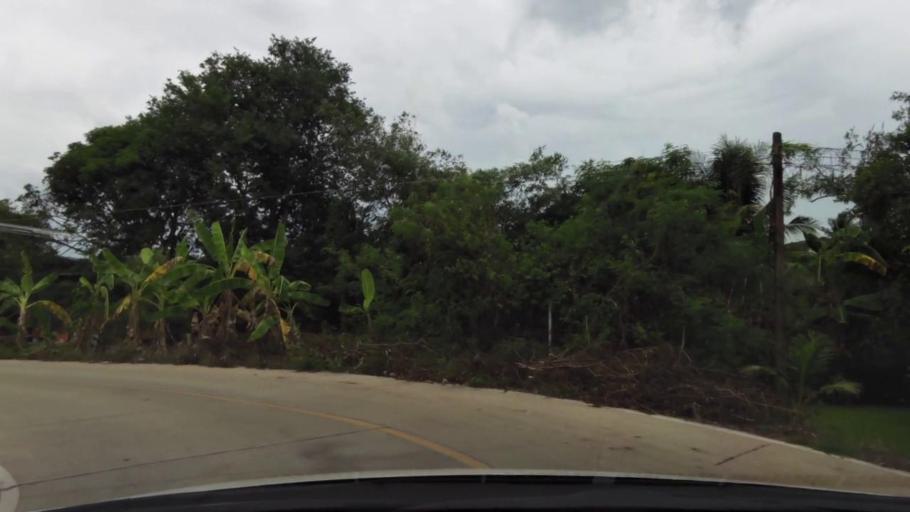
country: TH
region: Ratchaburi
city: Damnoen Saduak
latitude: 13.5614
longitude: 100.0193
